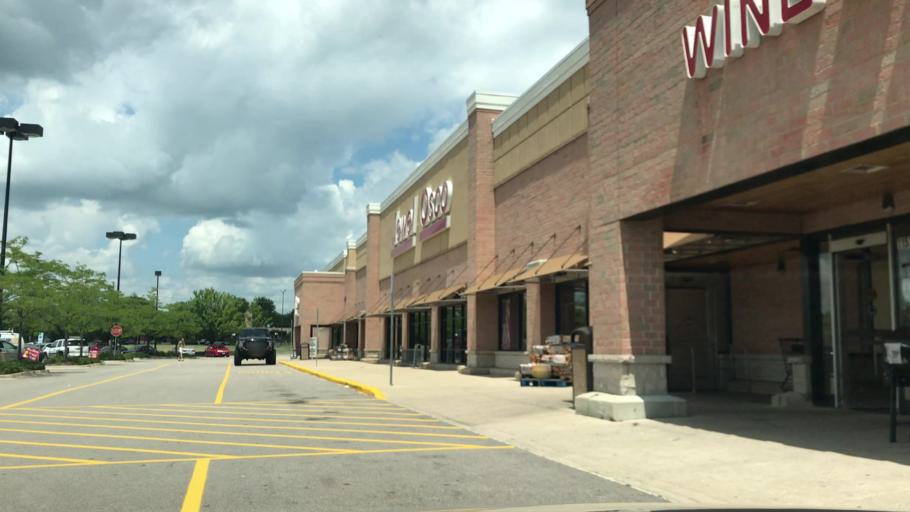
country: US
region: Illinois
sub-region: DuPage County
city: Warrenville
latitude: 41.7797
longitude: -88.2386
